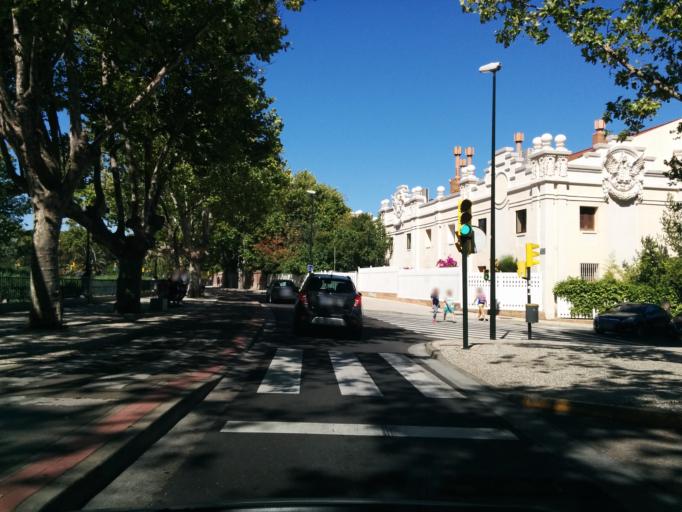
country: ES
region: Aragon
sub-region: Provincia de Zaragoza
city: Delicias
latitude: 41.6339
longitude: -0.8904
